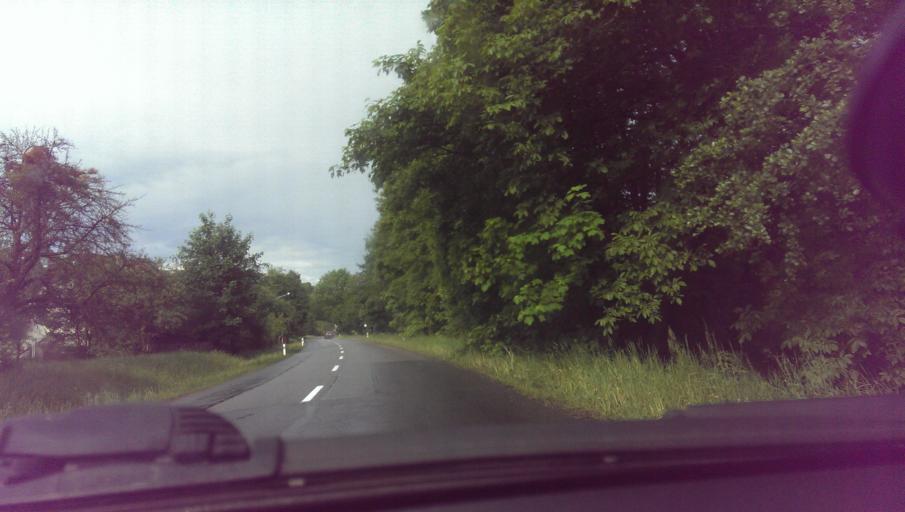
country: CZ
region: Zlin
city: Breznice
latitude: 49.1567
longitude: 17.6266
